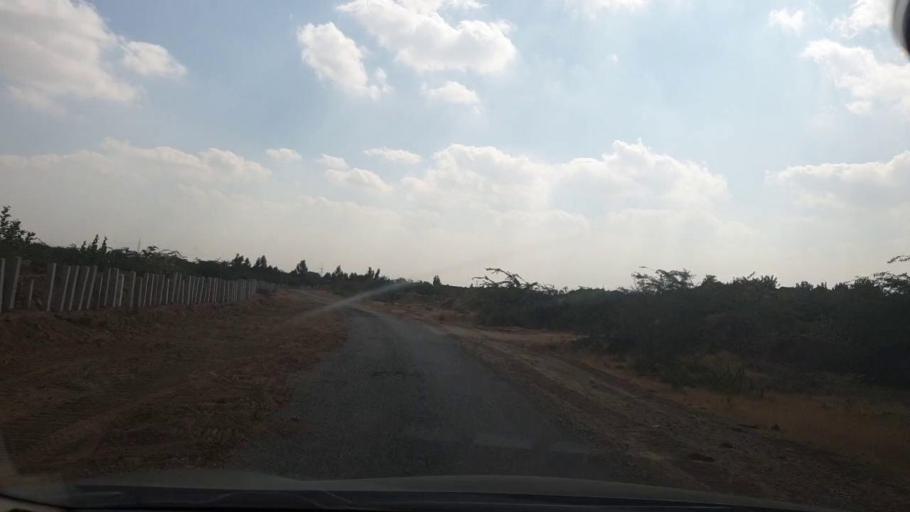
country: PK
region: Sindh
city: Malir Cantonment
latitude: 25.0237
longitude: 67.3534
